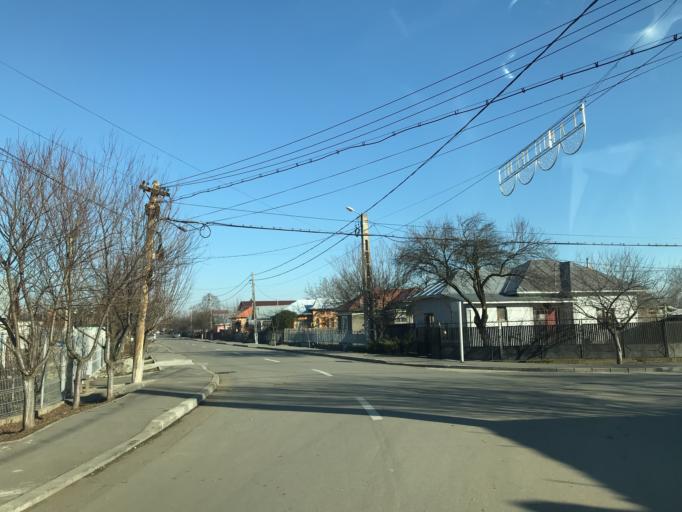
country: RO
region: Olt
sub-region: Municipiul Slatina
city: Slatina
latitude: 44.4520
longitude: 24.3687
